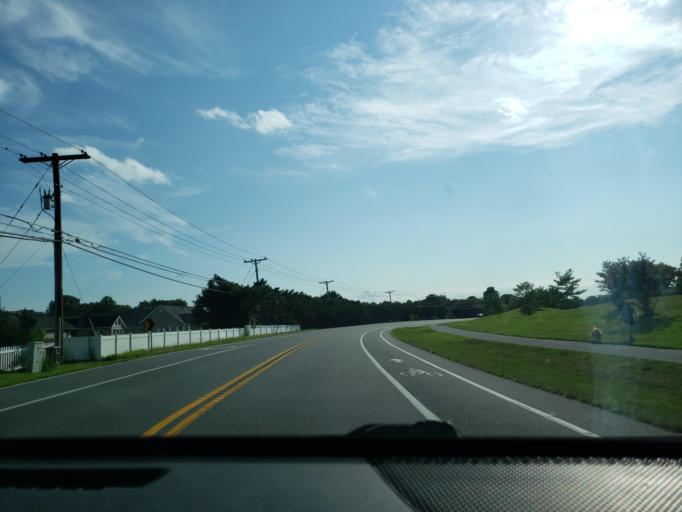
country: US
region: Delaware
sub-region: Sussex County
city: Milton
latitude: 38.7587
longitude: -75.2259
